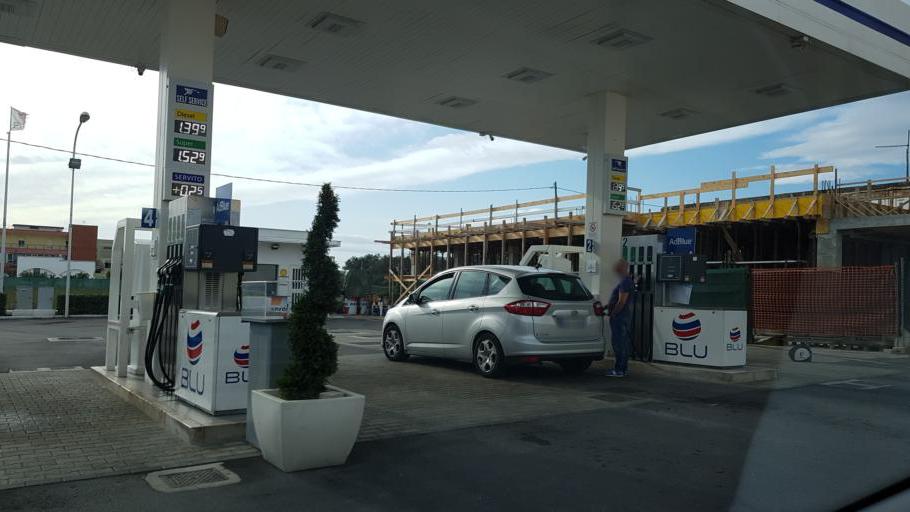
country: IT
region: Apulia
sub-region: Provincia di Brindisi
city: Mesagne
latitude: 40.5668
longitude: 17.8180
